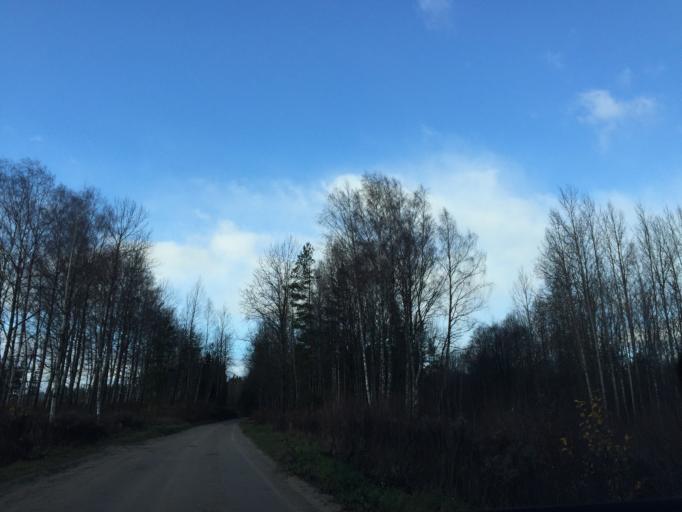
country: LV
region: Valmieras Rajons
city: Valmiera
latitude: 57.5385
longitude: 25.3816
